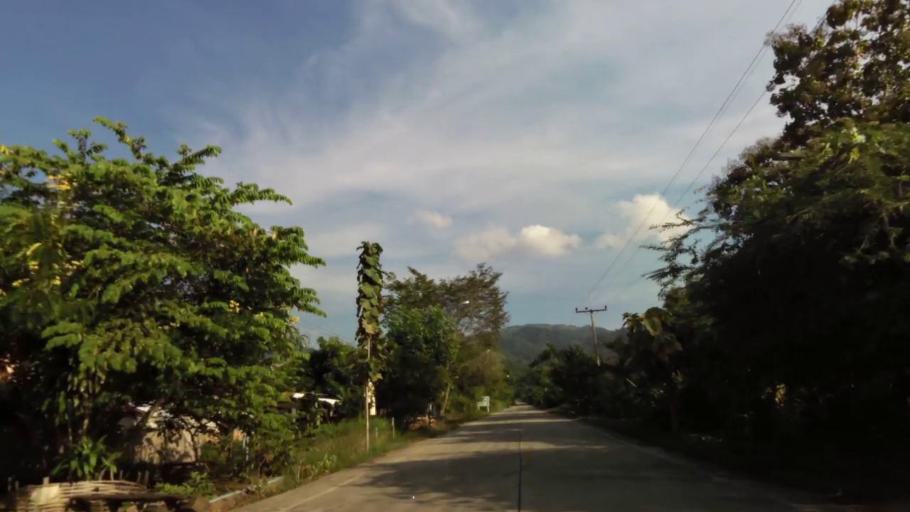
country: TH
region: Chiang Rai
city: Khun Tan
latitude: 19.8832
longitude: 100.2947
